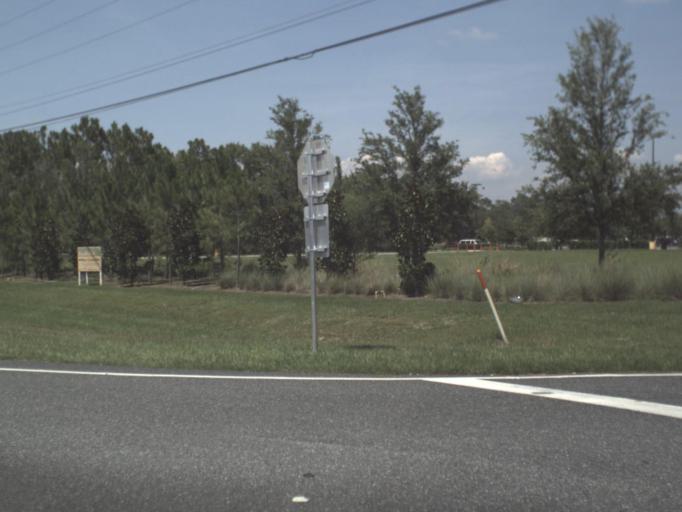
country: US
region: Florida
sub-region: Citrus County
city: Homosassa Springs
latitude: 28.7622
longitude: -82.5529
